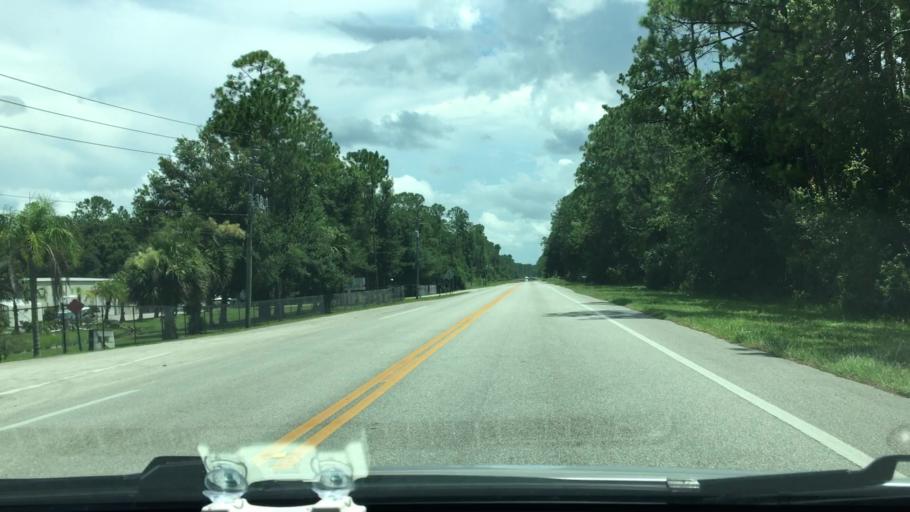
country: US
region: Florida
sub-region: Volusia County
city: Samsula-Spruce Creek
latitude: 29.0419
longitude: -81.0673
